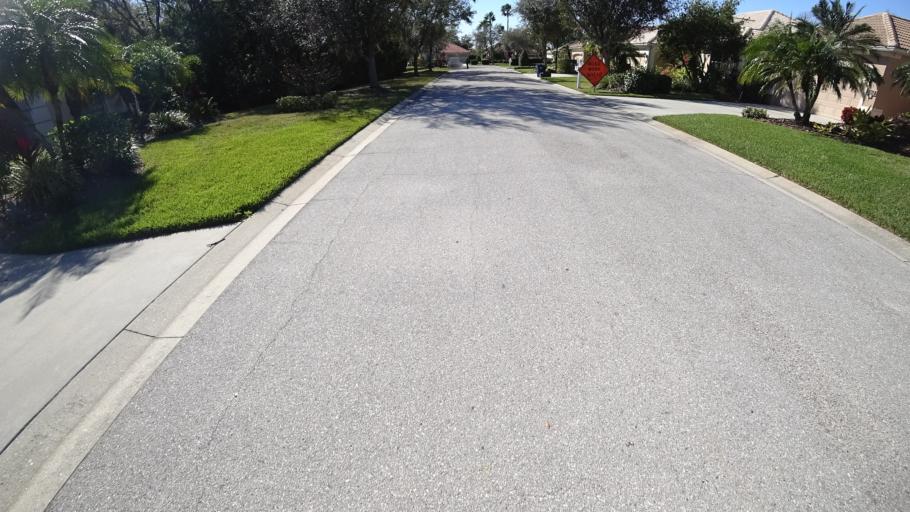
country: US
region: Florida
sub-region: Sarasota County
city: Desoto Lakes
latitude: 27.4287
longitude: -82.4640
